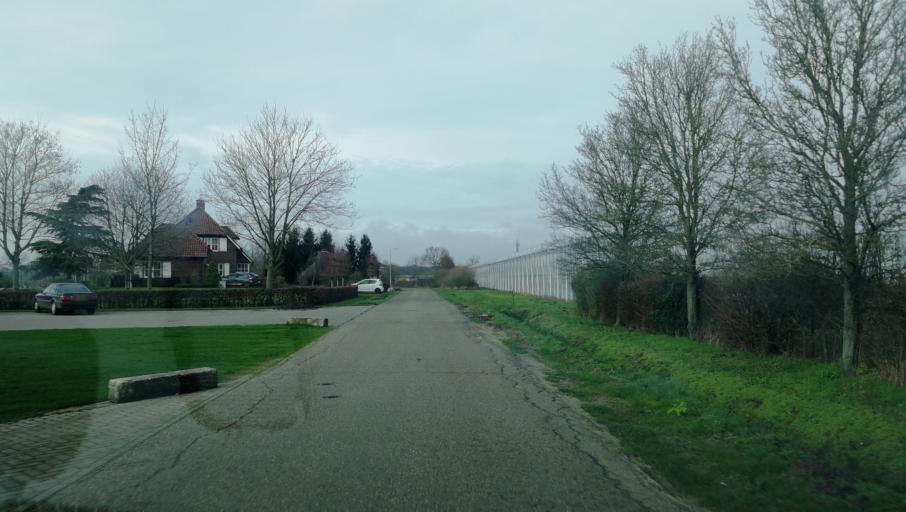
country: NL
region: Limburg
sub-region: Gemeente Beesel
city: Offenbeek
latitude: 51.2980
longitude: 6.1203
